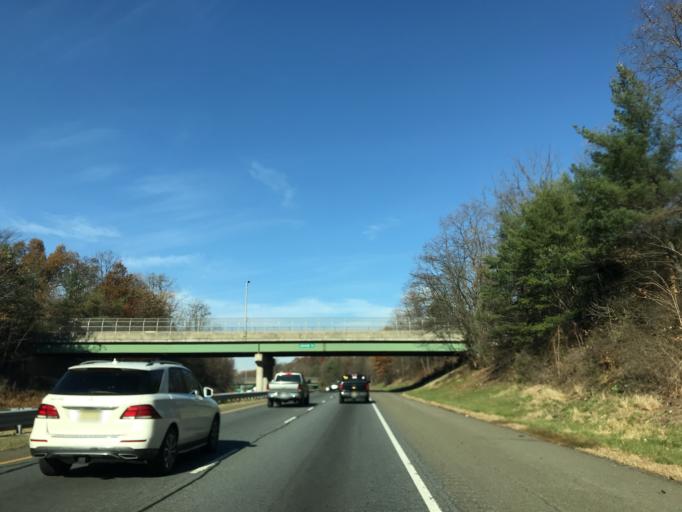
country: US
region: New Jersey
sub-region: Morris County
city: Madison
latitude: 40.7684
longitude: -74.4031
